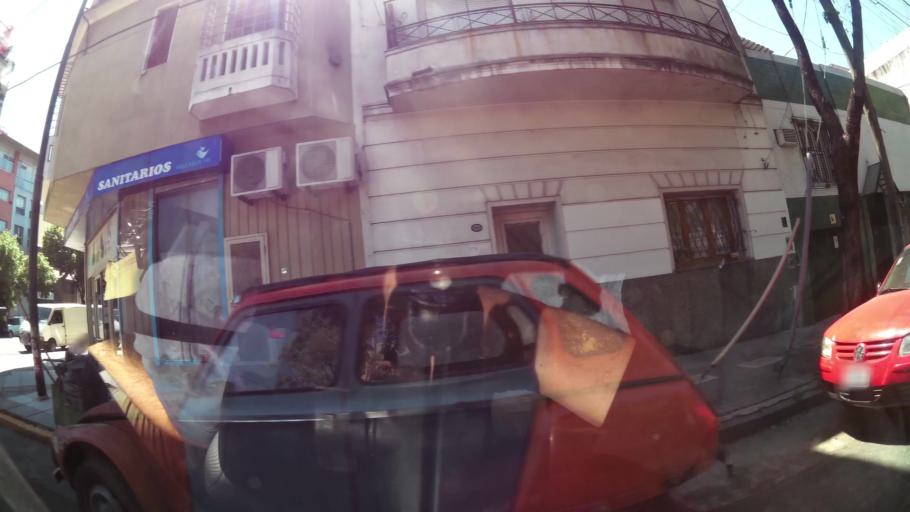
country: AR
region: Buenos Aires F.D.
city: Buenos Aires
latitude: -34.6320
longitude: -58.4192
